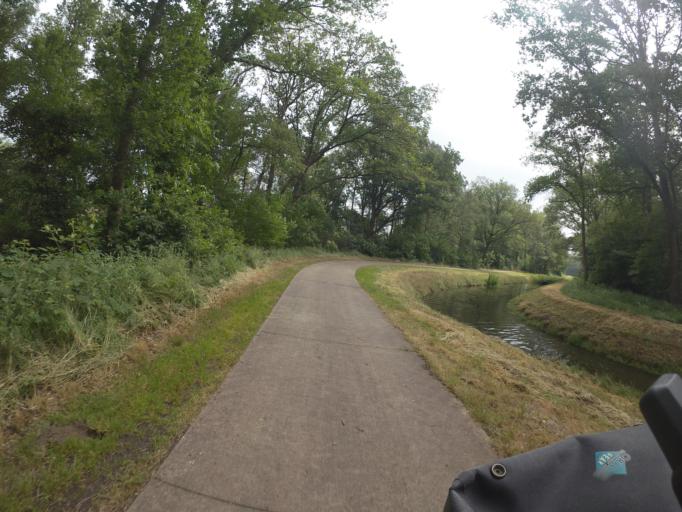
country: NL
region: Drenthe
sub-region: Gemeente Westerveld
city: Dwingeloo
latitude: 52.8376
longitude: 6.2996
